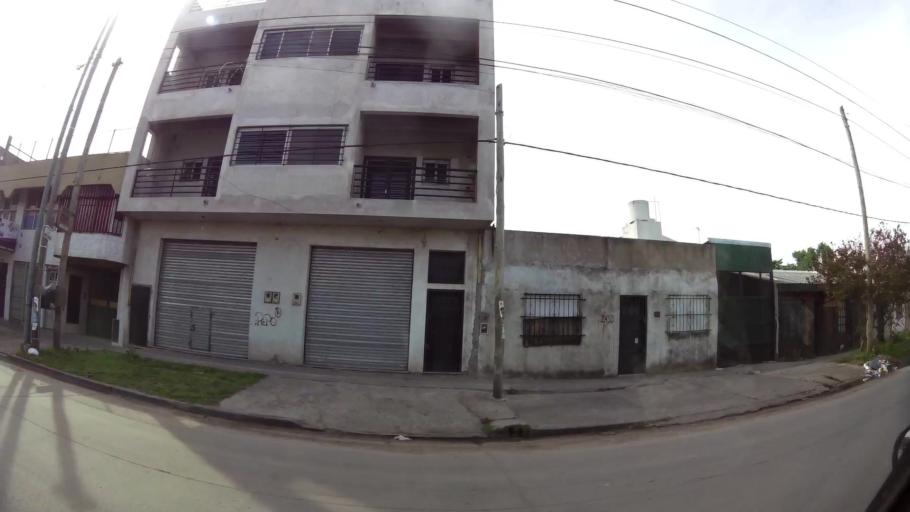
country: AR
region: Buenos Aires
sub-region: Partido de Quilmes
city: Quilmes
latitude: -34.7702
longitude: -58.2608
